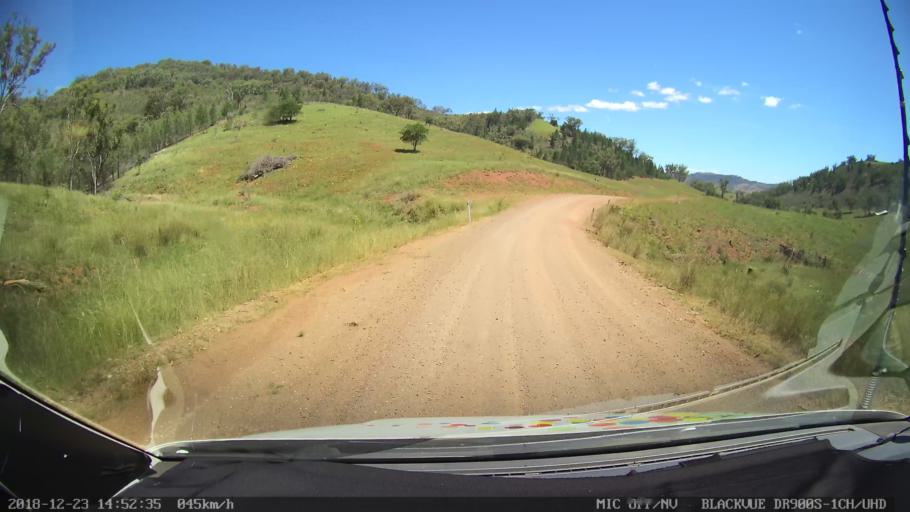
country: AU
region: New South Wales
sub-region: Tamworth Municipality
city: Manilla
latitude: -30.6853
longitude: 150.8545
